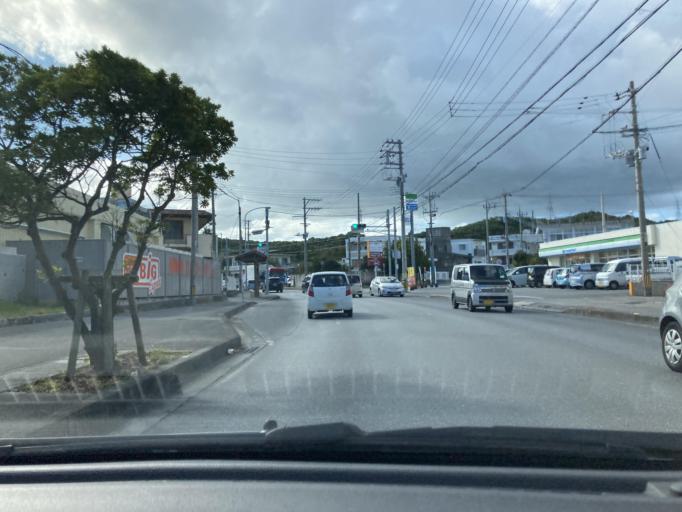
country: JP
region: Okinawa
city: Ginowan
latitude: 26.2269
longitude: 127.7625
